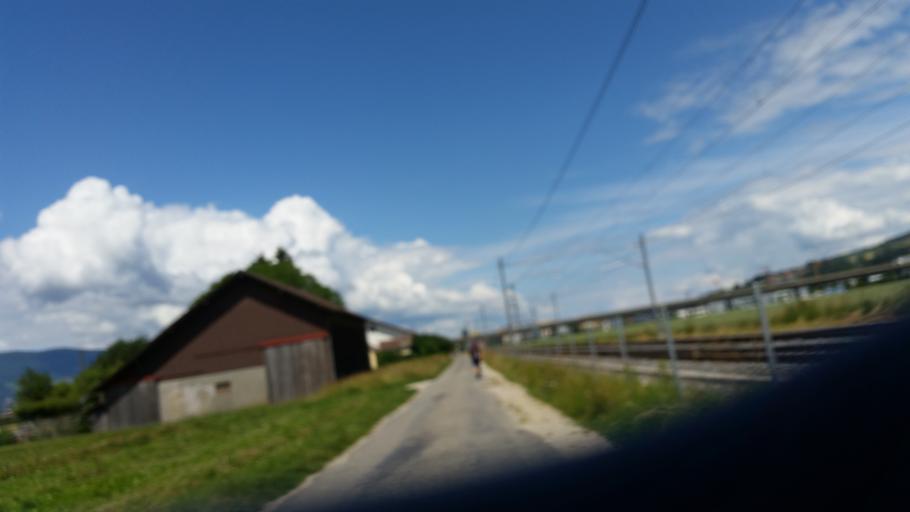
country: CH
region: Vaud
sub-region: Jura-Nord vaudois District
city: Yverdon-les-Bains
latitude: 46.7605
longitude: 6.6294
